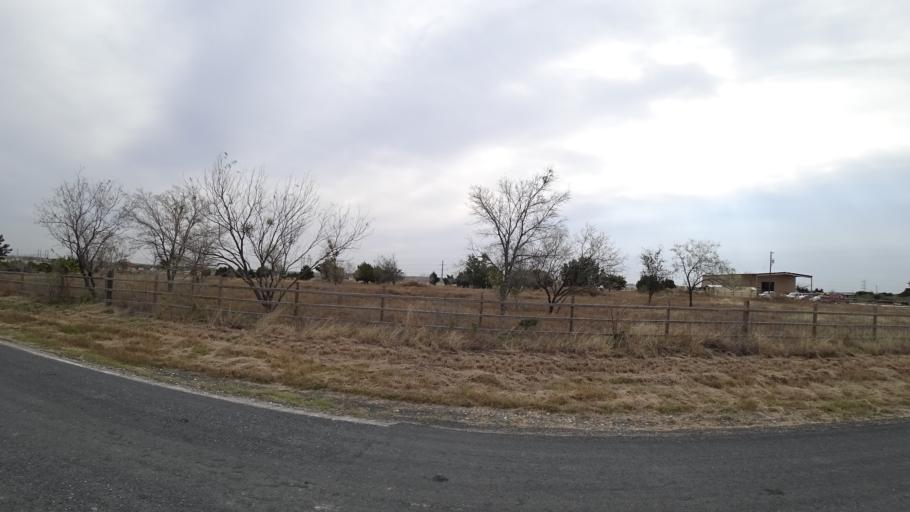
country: US
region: Texas
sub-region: Travis County
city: Garfield
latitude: 30.1563
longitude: -97.6602
